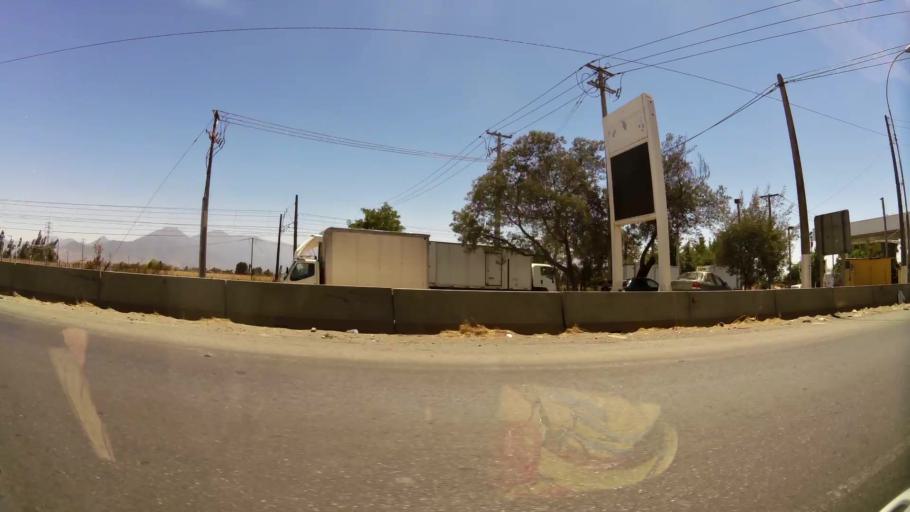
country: CL
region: O'Higgins
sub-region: Provincia de Cachapoal
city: Rancagua
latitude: -34.1906
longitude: -70.7527
